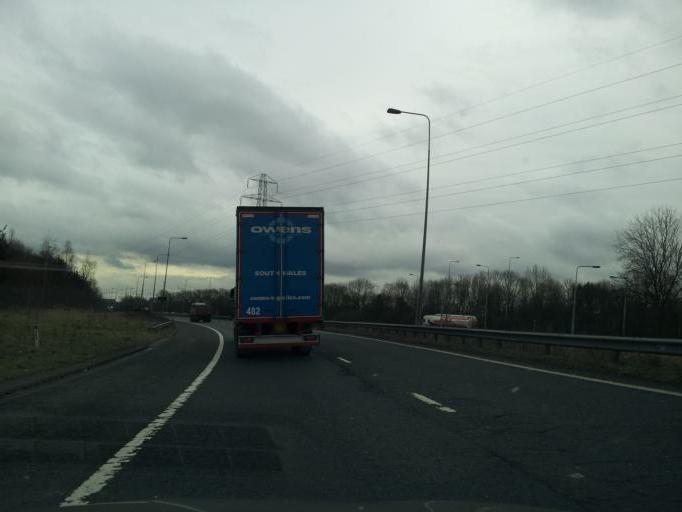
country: GB
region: England
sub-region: Warrington
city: Croft
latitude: 53.4224
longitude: -2.5484
